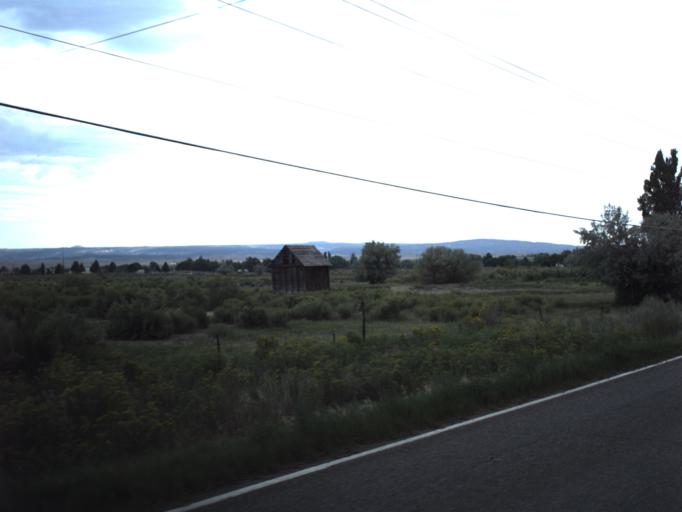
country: US
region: Utah
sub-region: Emery County
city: Huntington
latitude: 39.3573
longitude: -110.8521
